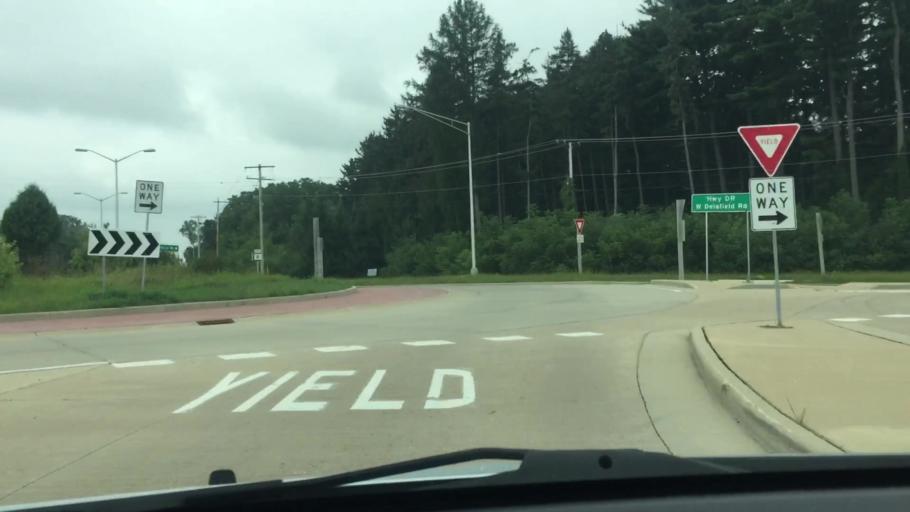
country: US
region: Wisconsin
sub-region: Waukesha County
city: Delafield
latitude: 43.0594
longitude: -88.4425
